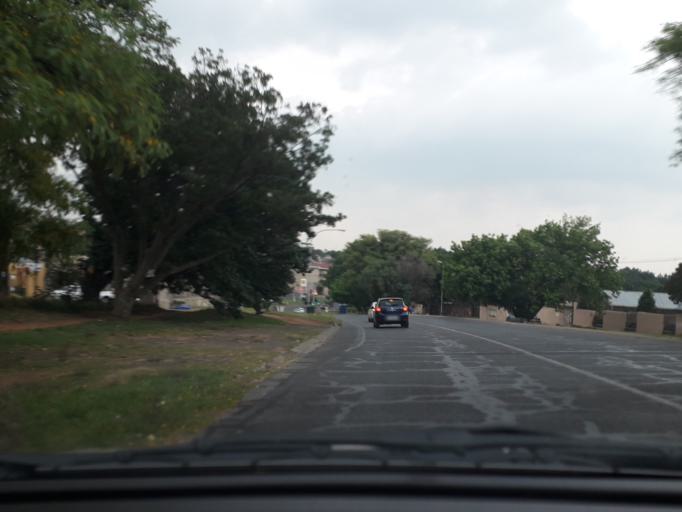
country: ZA
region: Gauteng
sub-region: City of Johannesburg Metropolitan Municipality
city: Johannesburg
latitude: -26.1475
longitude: 28.1026
